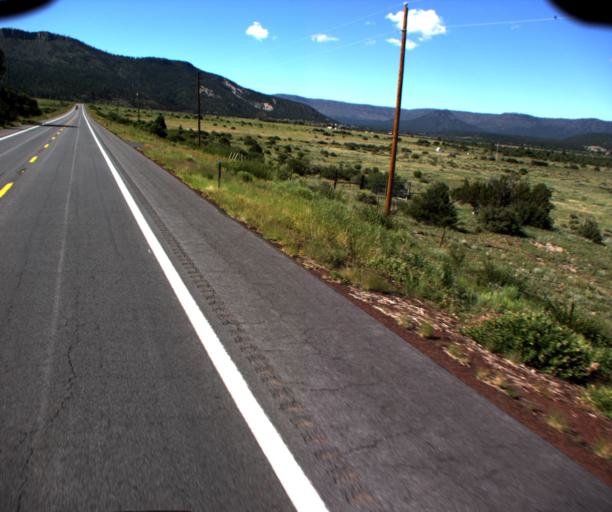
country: US
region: Arizona
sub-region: Apache County
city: Eagar
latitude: 33.9967
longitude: -109.1885
